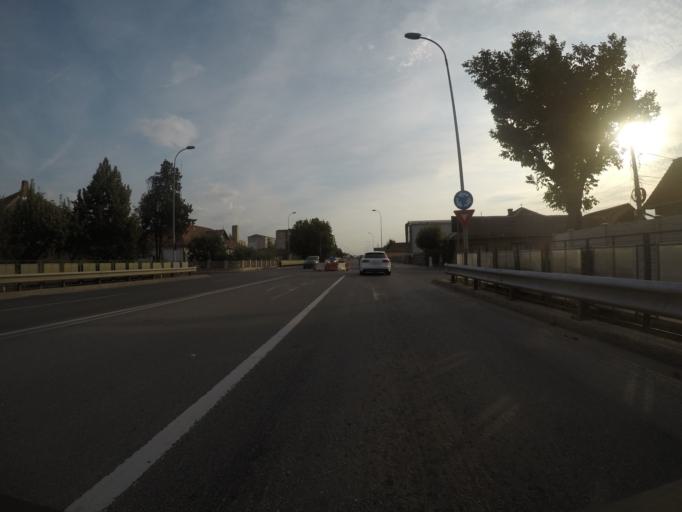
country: RO
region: Alba
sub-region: Municipiul Alba Iulia
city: Barabant
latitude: 46.0926
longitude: 23.5957
